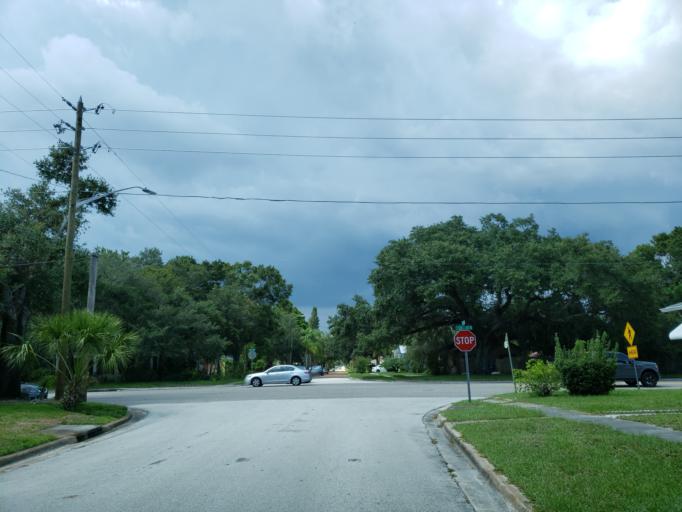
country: US
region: Florida
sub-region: Pinellas County
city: Lealman
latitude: 27.8064
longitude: -82.6427
